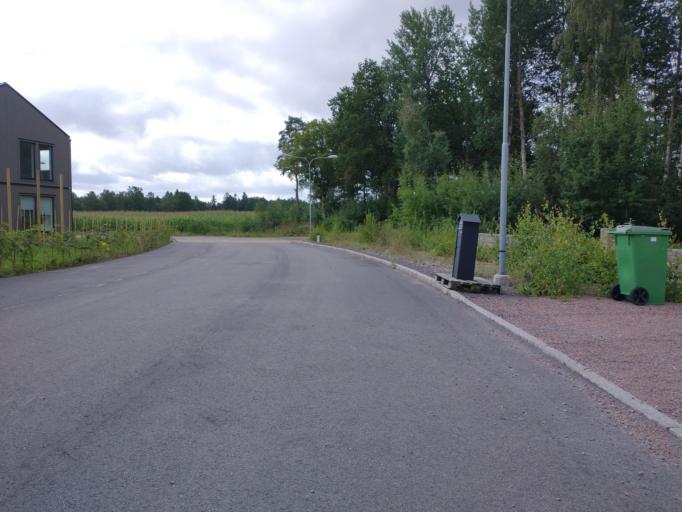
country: SE
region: Kalmar
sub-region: Kalmar Kommun
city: Lindsdal
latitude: 56.7786
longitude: 16.3003
